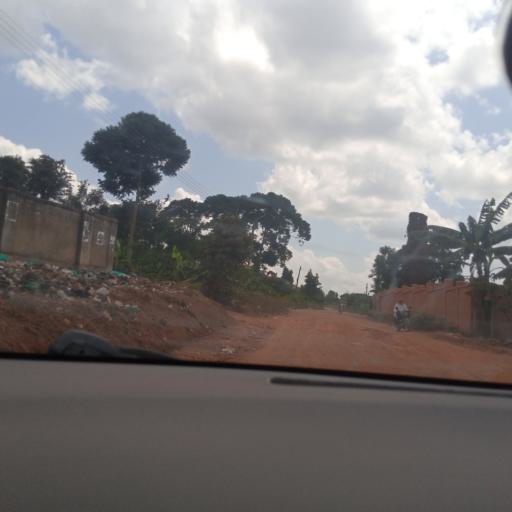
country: UG
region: Central Region
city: Masaka
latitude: -0.3219
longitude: 31.7473
